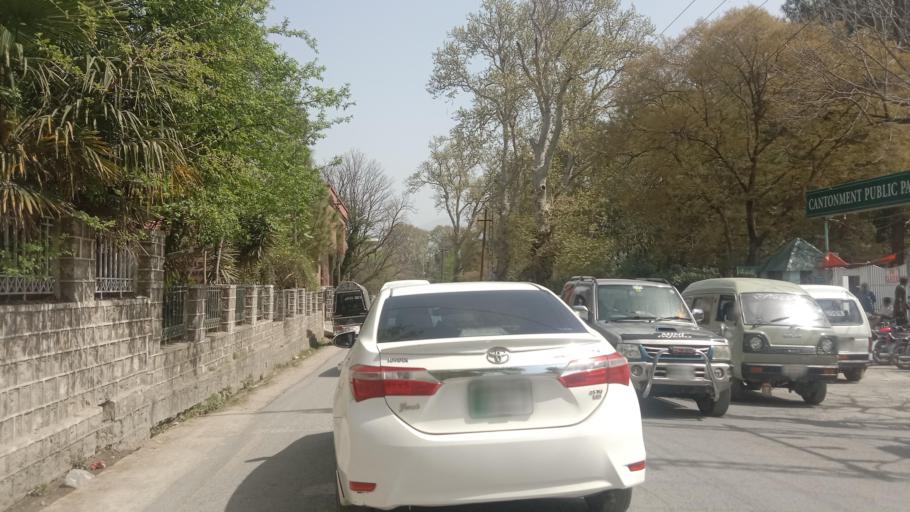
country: PK
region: Khyber Pakhtunkhwa
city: Abbottabad
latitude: 34.1505
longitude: 73.2148
